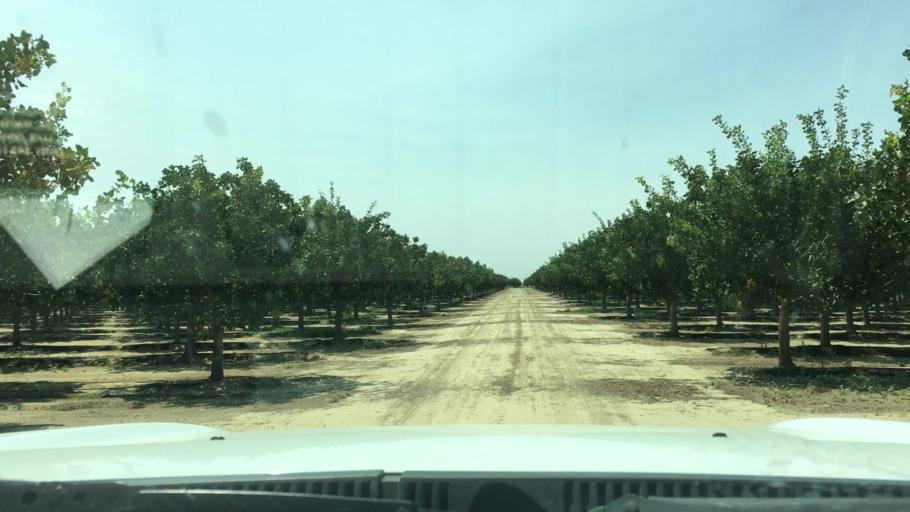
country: US
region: California
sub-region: Tulare County
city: Earlimart
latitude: 35.8221
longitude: -119.3619
